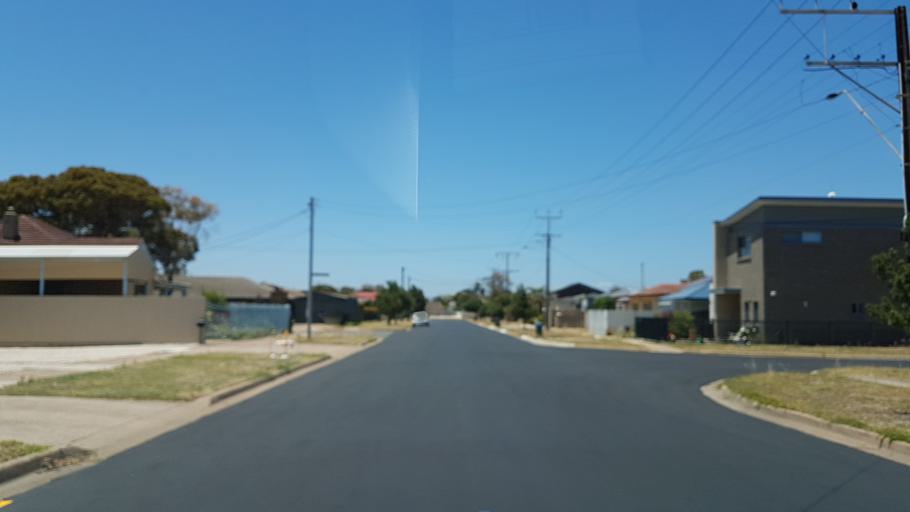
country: AU
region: South Australia
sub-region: Charles Sturt
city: West Lakes Shore
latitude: -34.8593
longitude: 138.4813
